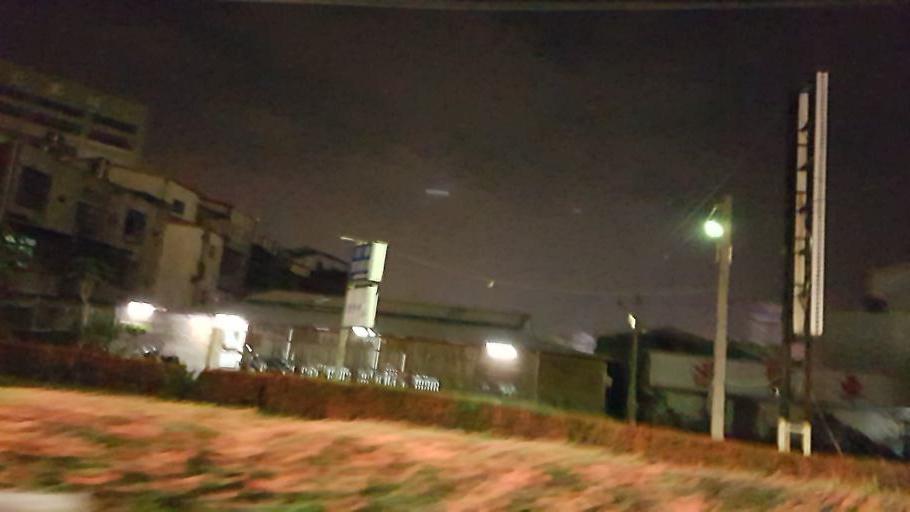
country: TW
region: Taiwan
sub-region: Changhua
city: Chang-hua
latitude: 24.0675
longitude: 120.5258
